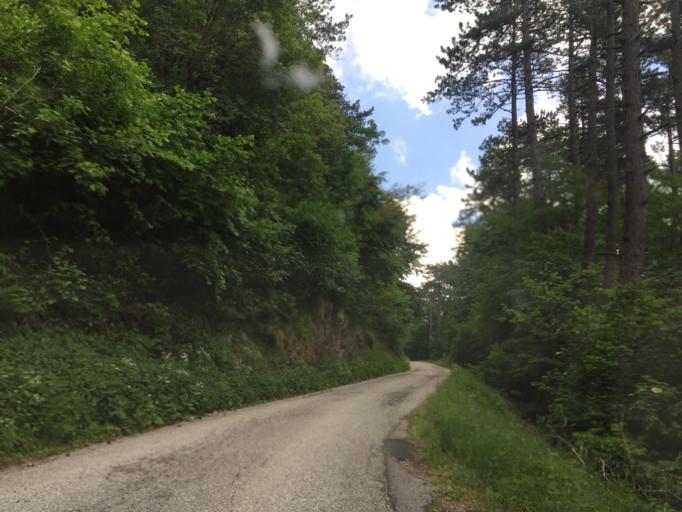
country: SI
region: Nova Gorica
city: Sempas
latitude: 46.0239
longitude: 13.7480
